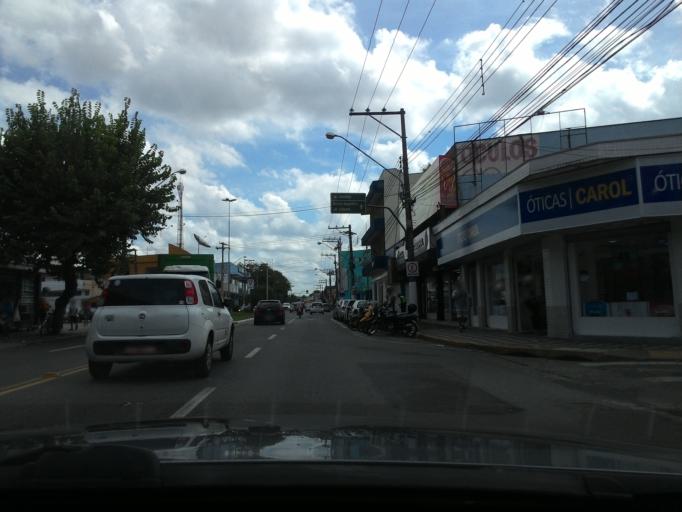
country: BR
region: Sao Paulo
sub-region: Registro
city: Registro
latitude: -24.4960
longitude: -47.8469
